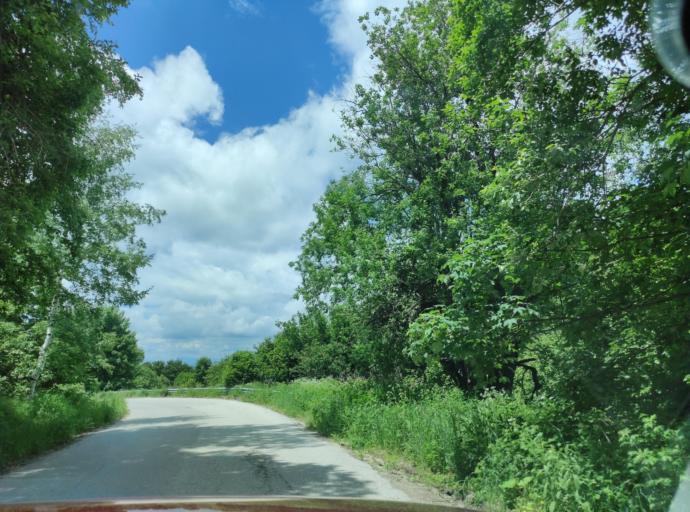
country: BG
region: Sofia-Capital
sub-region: Stolichna Obshtina
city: Sofia
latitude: 42.6343
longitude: 23.2384
